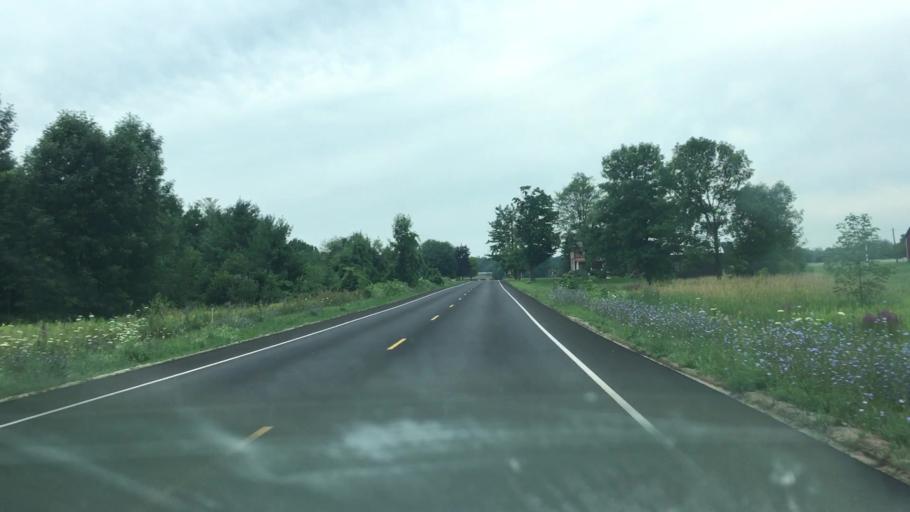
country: US
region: New York
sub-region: Clinton County
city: Morrisonville
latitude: 44.6489
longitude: -73.5619
